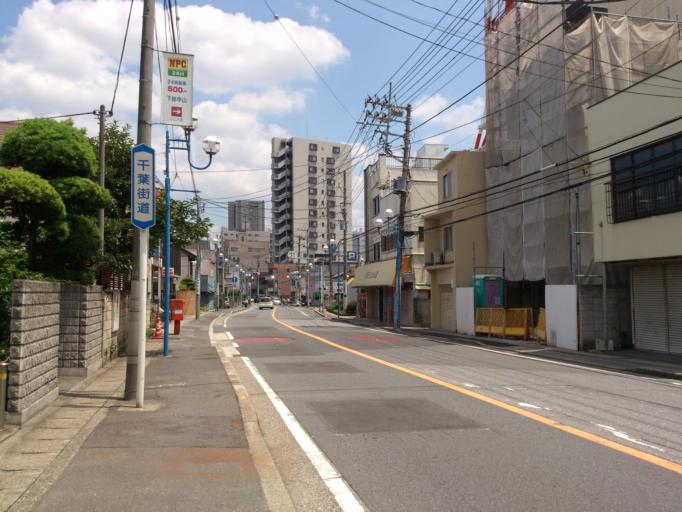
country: JP
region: Chiba
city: Funabashi
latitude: 35.7169
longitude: 139.9415
